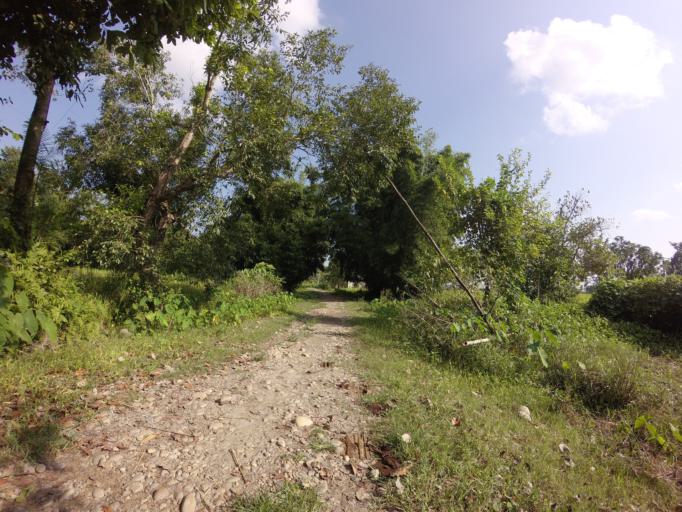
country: NP
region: Far Western
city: Tikapur
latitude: 28.4397
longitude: 81.0751
